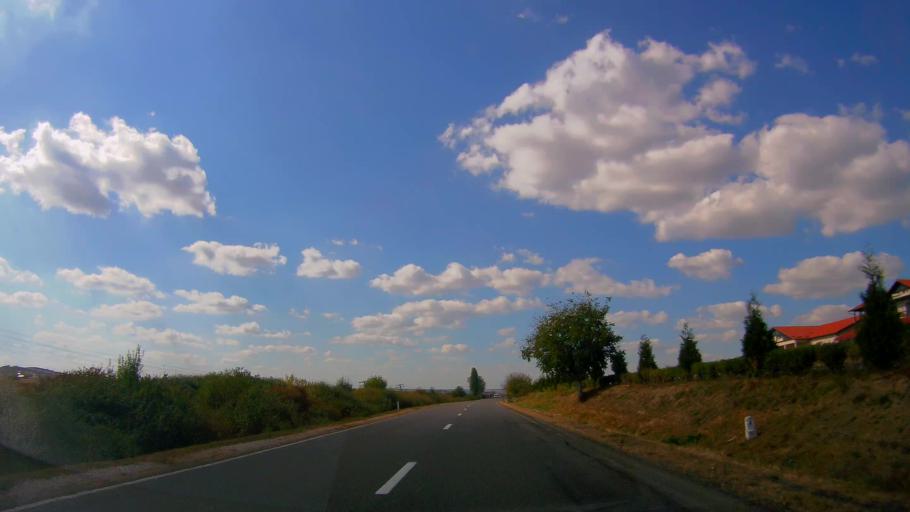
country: RO
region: Salaj
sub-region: Comuna Sarmasag
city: Sarmasag
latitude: 47.3304
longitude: 22.8603
